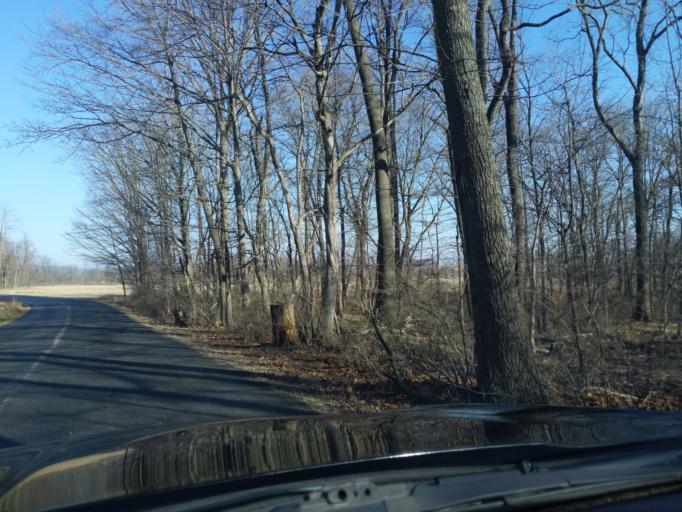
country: US
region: Pennsylvania
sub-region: Blair County
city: Bellwood
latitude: 40.5797
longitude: -78.2733
